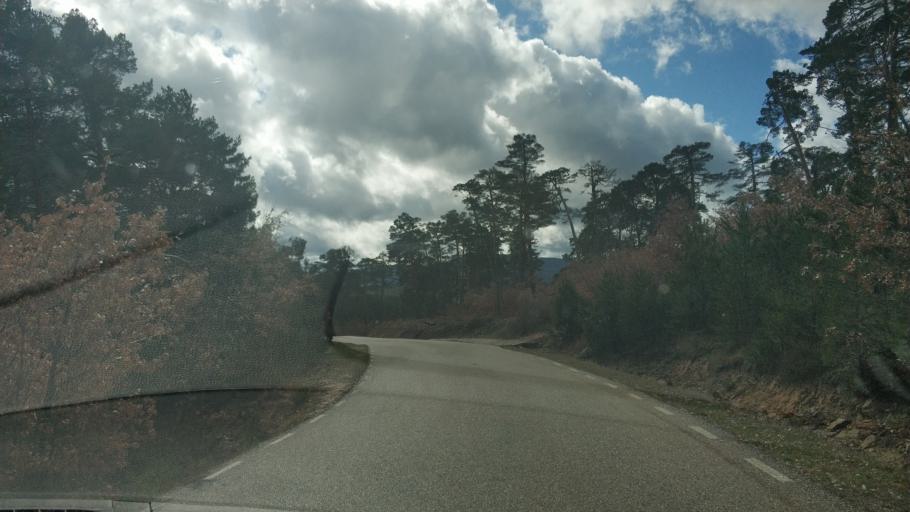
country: ES
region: Castille and Leon
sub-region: Provincia de Burgos
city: Quintanar de la Sierra
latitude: 41.9960
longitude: -3.0205
